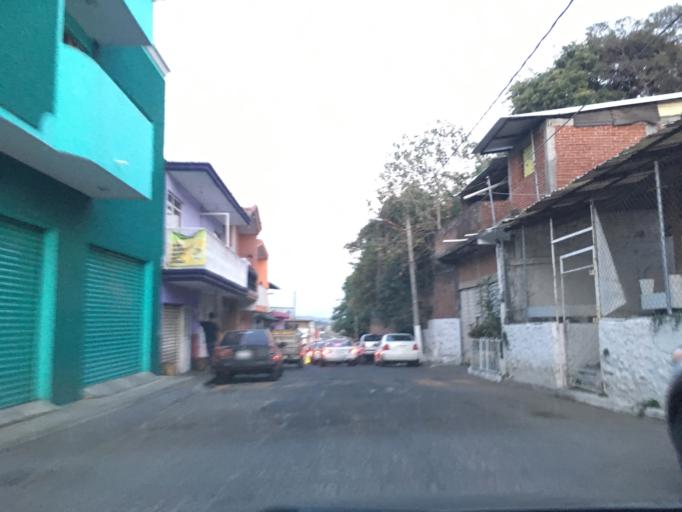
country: MX
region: Michoacan
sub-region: Uruapan
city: Uruapan
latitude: 19.4134
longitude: -102.0673
